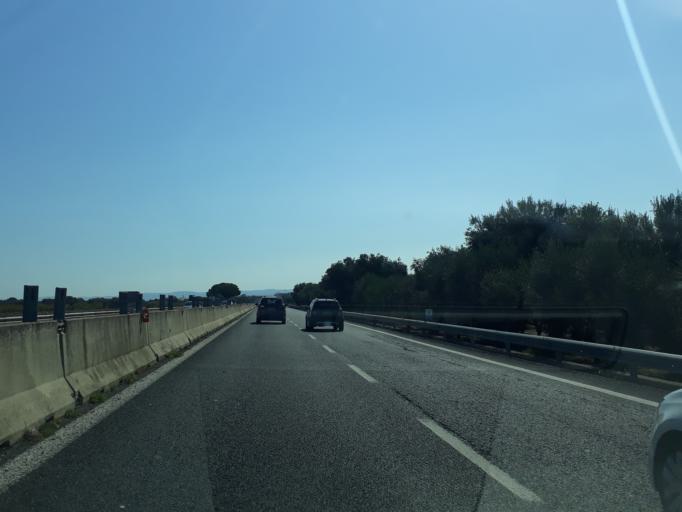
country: IT
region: Apulia
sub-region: Provincia di Bari
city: Monopoli
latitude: 40.9144
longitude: 17.3204
